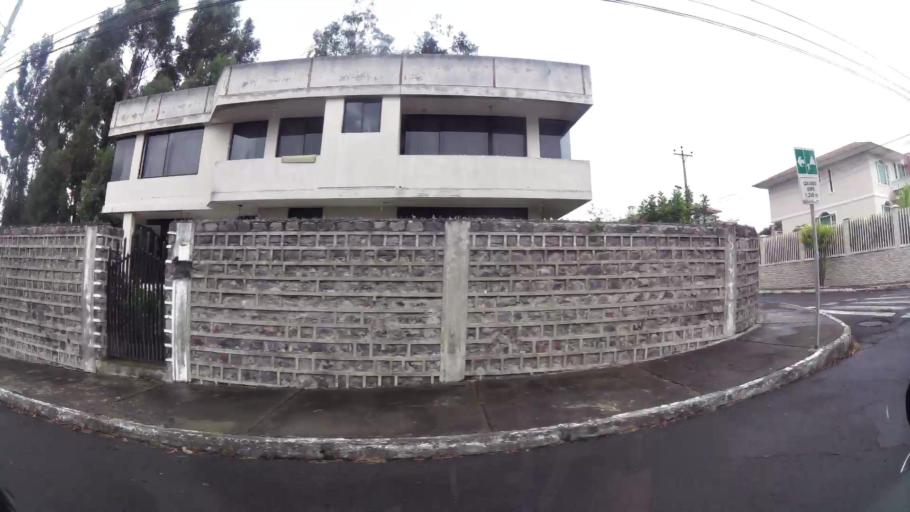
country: EC
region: Pichincha
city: Sangolqui
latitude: -0.3190
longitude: -78.4359
